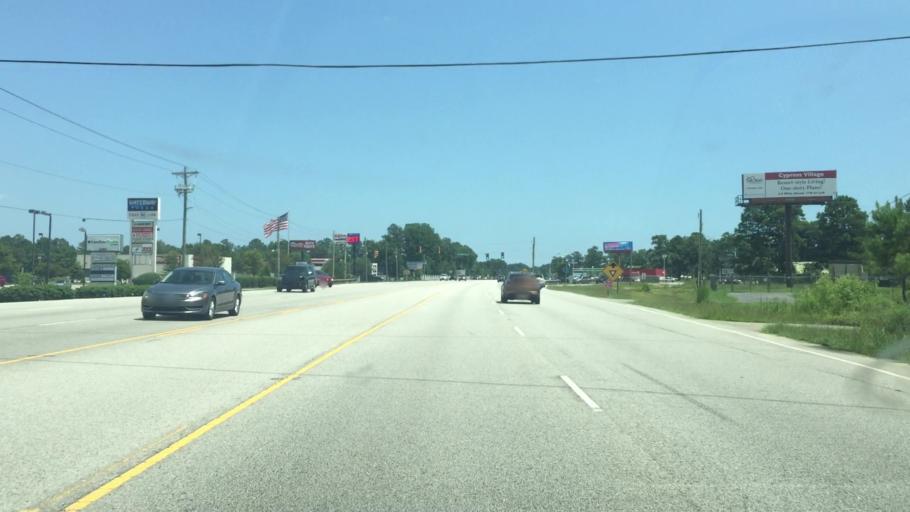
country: US
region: South Carolina
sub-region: Horry County
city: North Myrtle Beach
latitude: 33.8727
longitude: -78.6749
